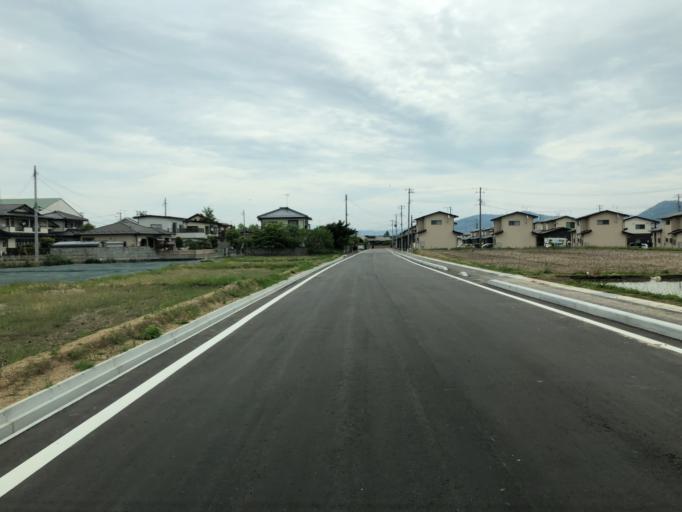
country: JP
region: Fukushima
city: Fukushima-shi
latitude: 37.7884
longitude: 140.4301
